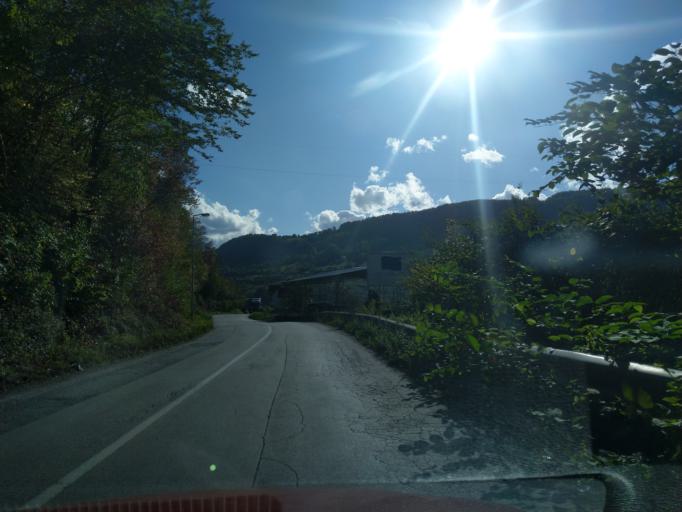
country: RS
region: Central Serbia
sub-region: Zlatiborski Okrug
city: Uzice
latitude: 43.8653
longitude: 19.8145
